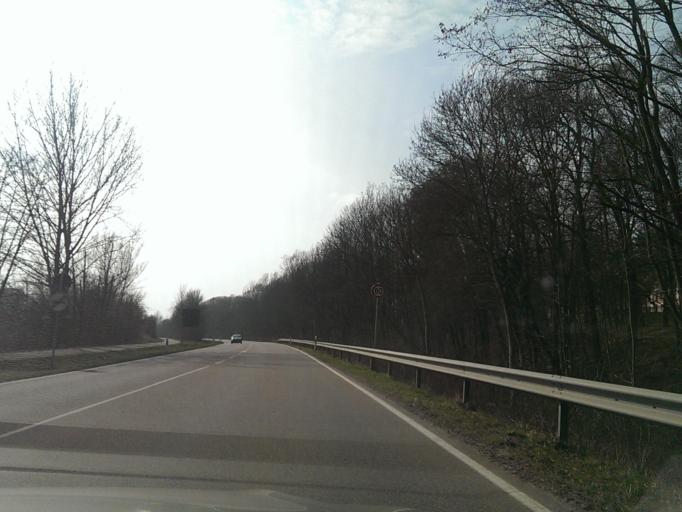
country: DE
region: Bavaria
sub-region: Upper Palatinate
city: Donaustauf
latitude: 49.0294
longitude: 12.2161
